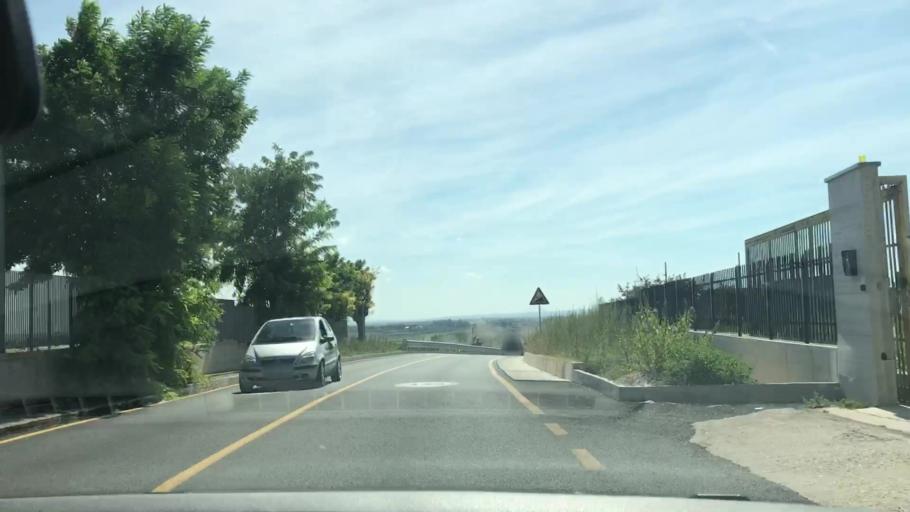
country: IT
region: Apulia
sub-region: Provincia di Bari
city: Altamura
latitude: 40.8108
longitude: 16.5548
